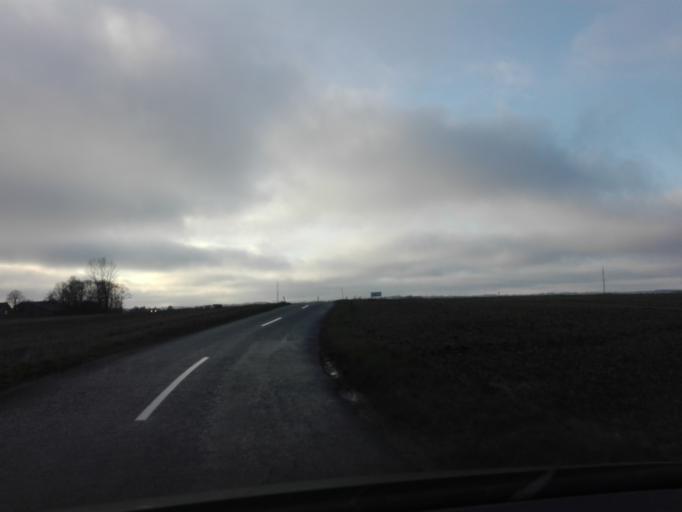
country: DK
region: Central Jutland
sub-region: Arhus Kommune
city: Solbjerg
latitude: 56.0376
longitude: 10.1103
